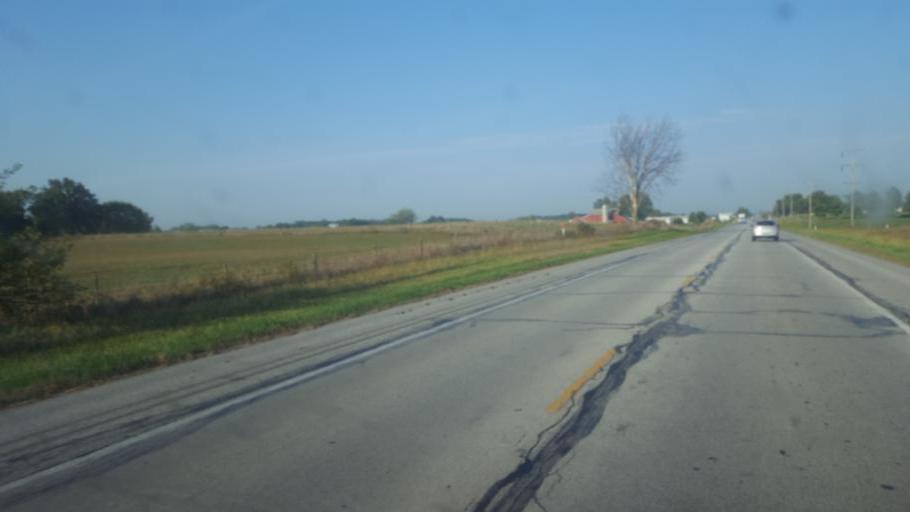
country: US
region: Indiana
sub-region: LaGrange County
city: Lagrange
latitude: 41.6410
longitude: -85.4856
